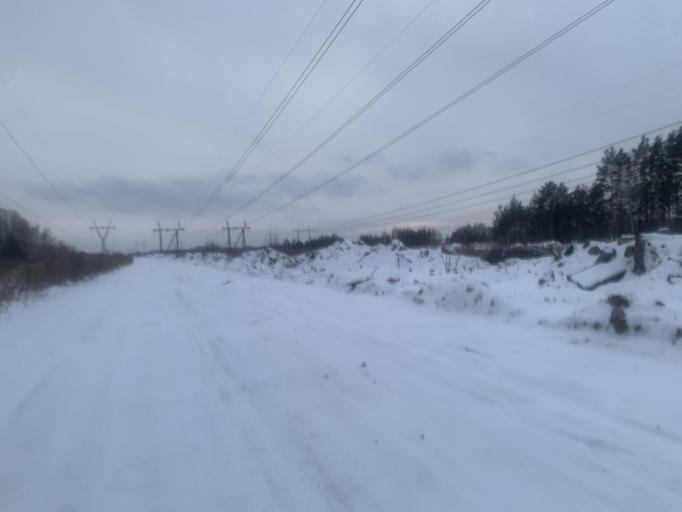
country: RU
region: Chelyabinsk
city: Roshchino
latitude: 55.1951
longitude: 61.2605
